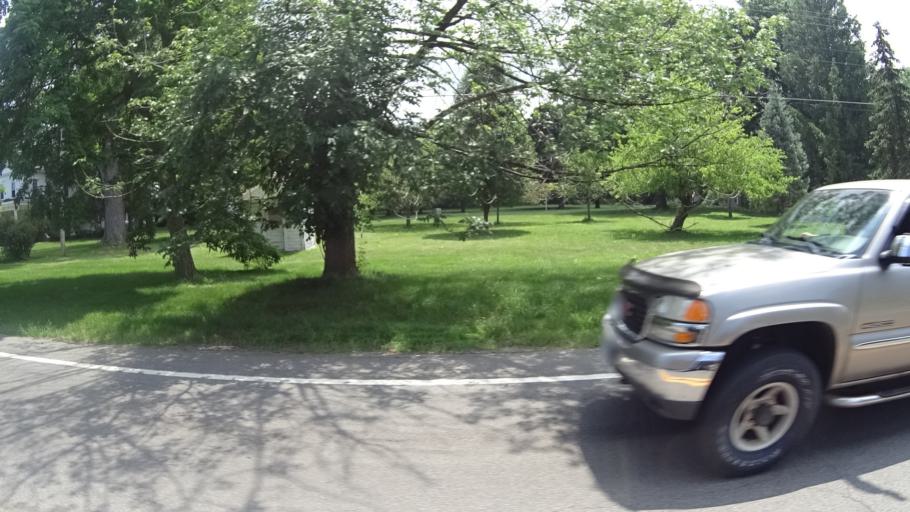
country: US
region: Ohio
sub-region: Lorain County
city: Vermilion
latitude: 41.4002
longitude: -82.4230
